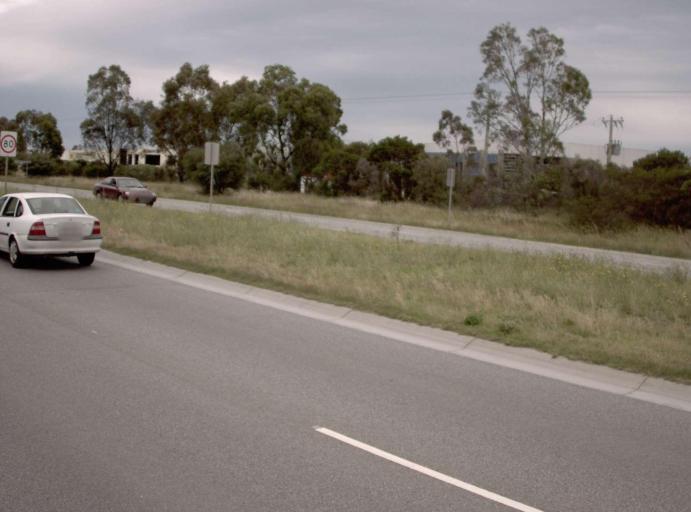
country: AU
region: Victoria
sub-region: Casey
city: Hampton Park
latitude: -38.0308
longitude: 145.2443
